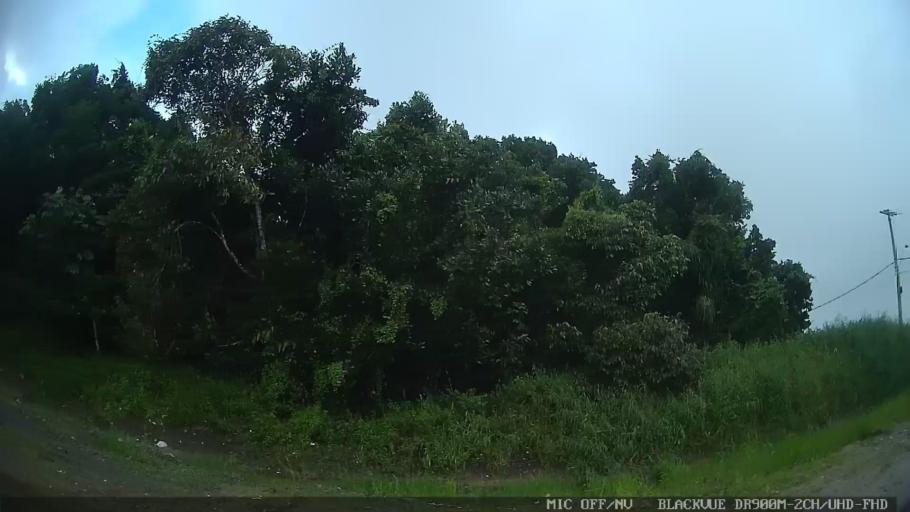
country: BR
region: Sao Paulo
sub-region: Itanhaem
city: Itanhaem
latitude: -24.1997
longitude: -46.8296
